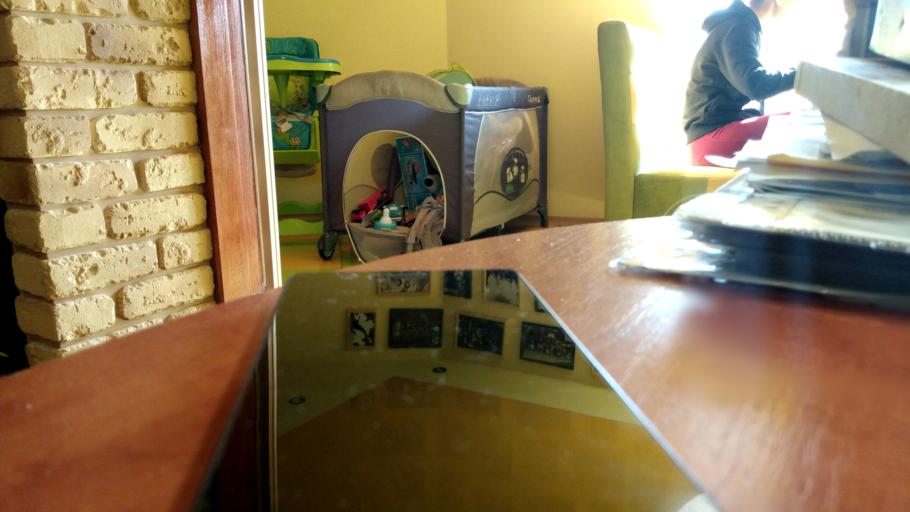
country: RU
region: Penza
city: Serdobsk
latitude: 52.4721
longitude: 44.2768
